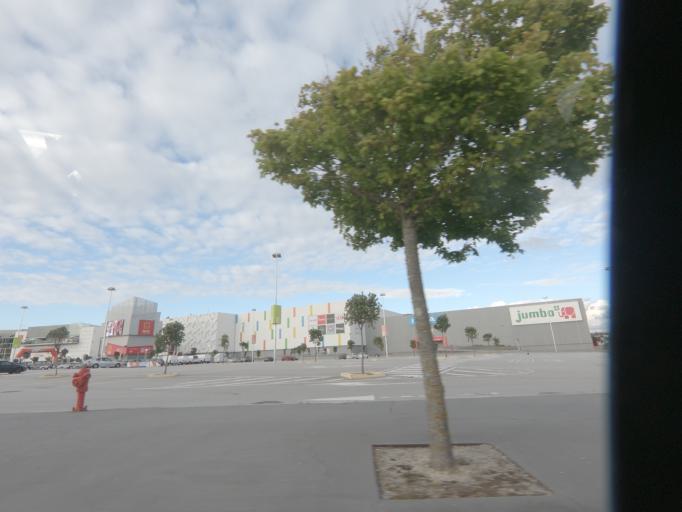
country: PT
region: Porto
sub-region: Matosinhos
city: Santa Cruz do Bispo
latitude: 41.2072
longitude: -8.6893
